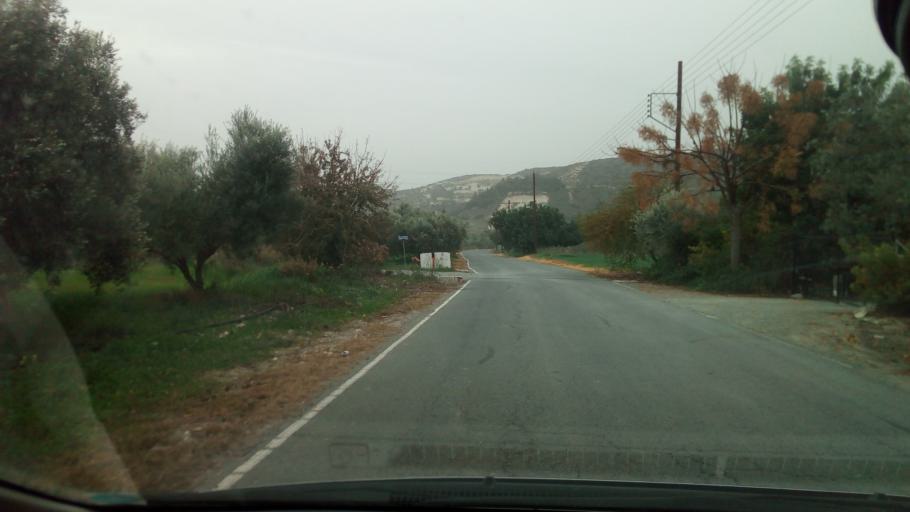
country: CY
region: Limassol
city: Pyrgos
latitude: 34.7262
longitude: 33.2305
